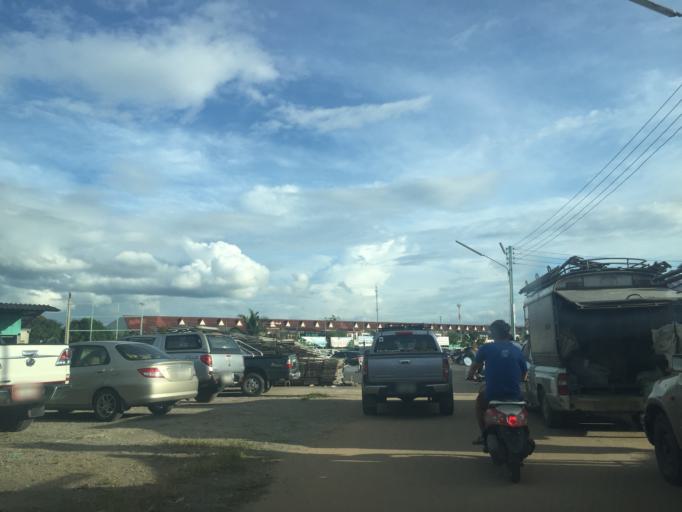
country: TH
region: Lamphun
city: Lamphun
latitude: 18.5580
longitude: 99.0372
